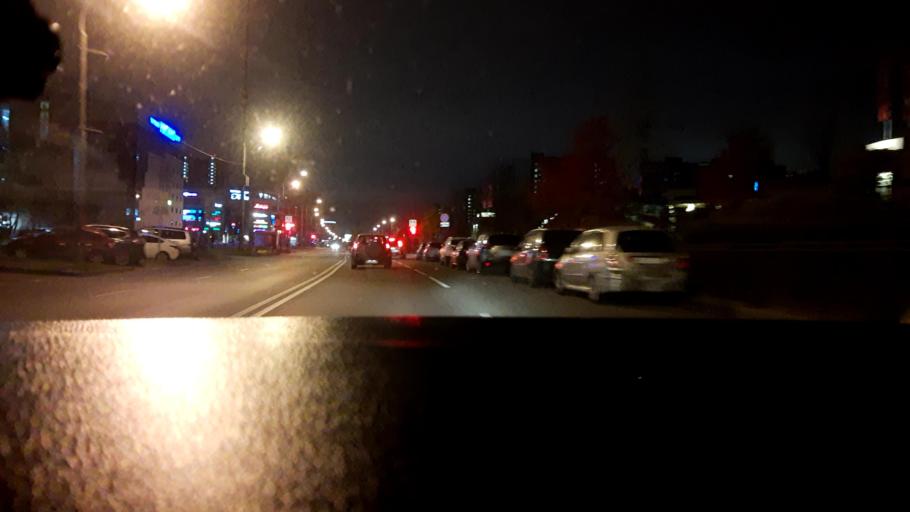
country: RU
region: Moskovskaya
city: Pavshino
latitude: 55.8479
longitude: 37.3575
